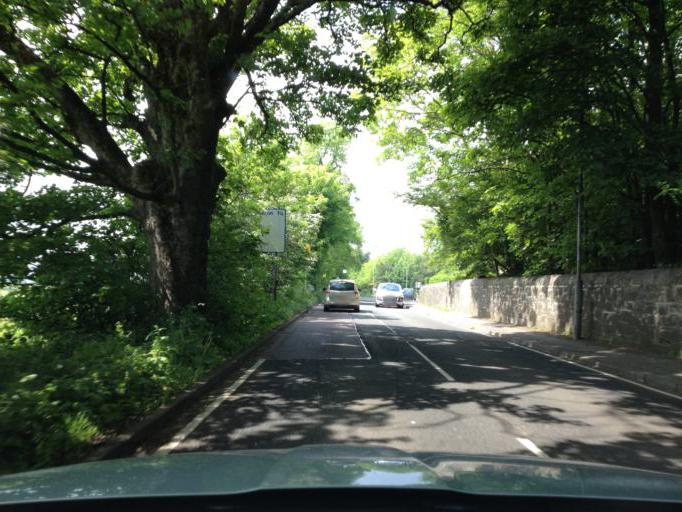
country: GB
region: Scotland
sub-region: West Dunbartonshire
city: Old Kilpatrick
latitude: 55.9142
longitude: -4.4788
